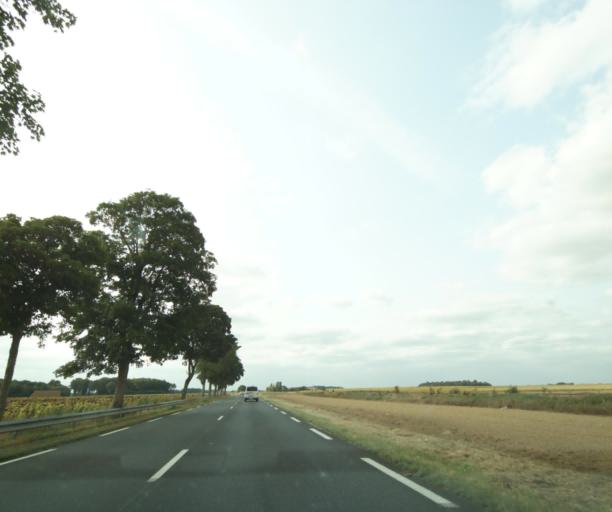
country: FR
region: Centre
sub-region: Departement d'Indre-et-Loire
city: Truyes
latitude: 47.2398
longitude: 0.8641
